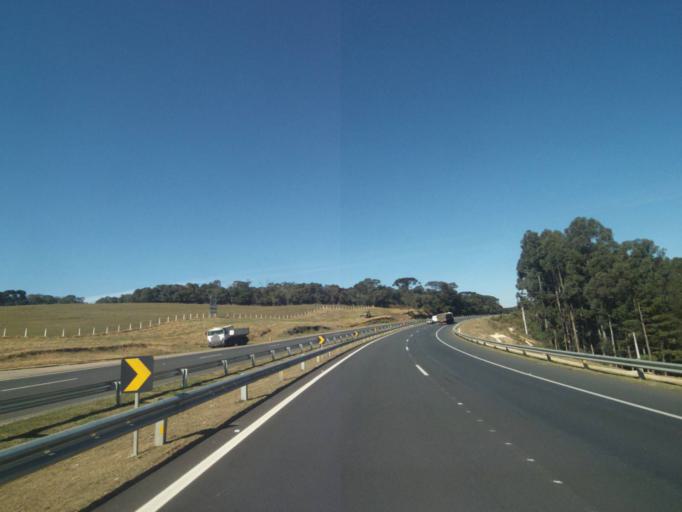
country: BR
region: Parana
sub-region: Carambei
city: Carambei
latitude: -24.9020
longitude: -50.4231
